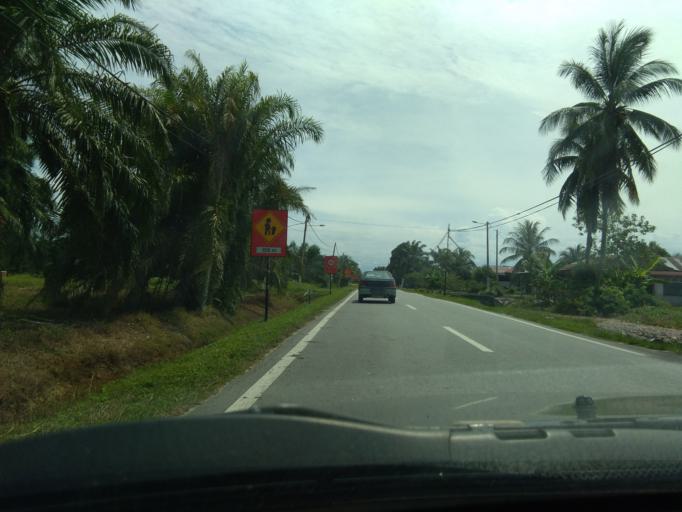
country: MY
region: Perak
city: Bagan Serai
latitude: 5.0389
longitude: 100.5713
